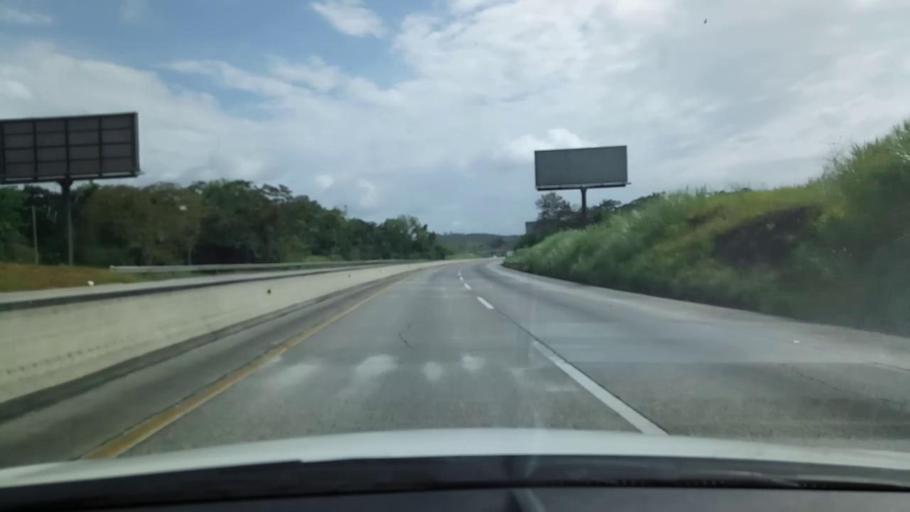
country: PA
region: Colon
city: El Giral
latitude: 9.2572
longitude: -79.6930
